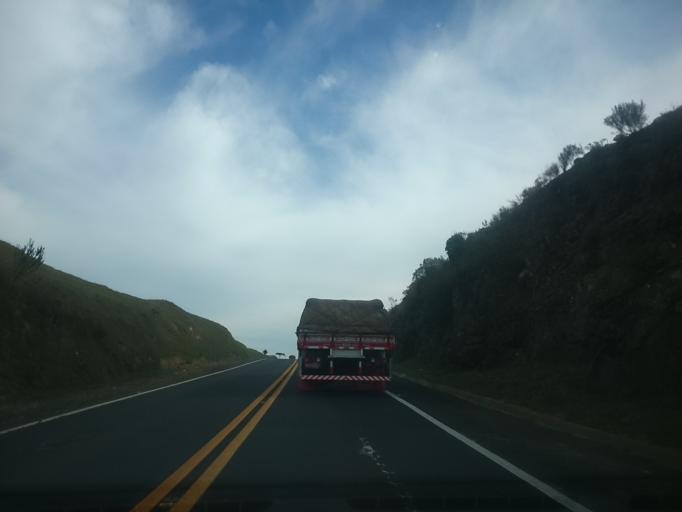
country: BR
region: Rio Grande do Sul
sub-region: Vacaria
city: Estrela
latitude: -28.1060
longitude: -50.6160
